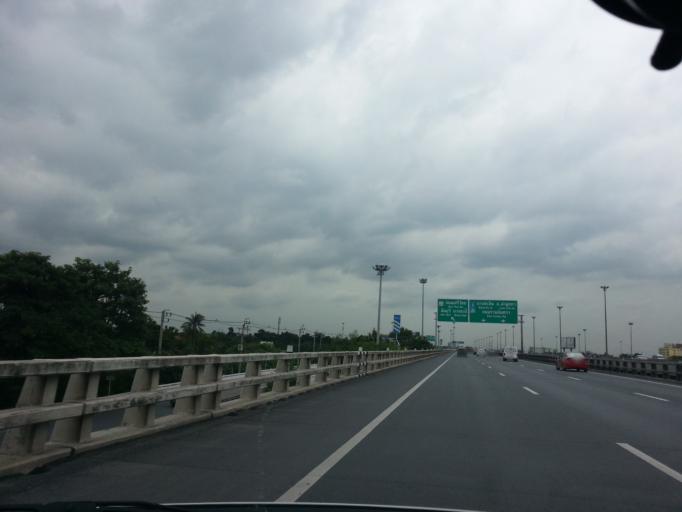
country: TH
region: Bangkok
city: Bueng Kum
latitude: 13.7850
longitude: 100.6844
